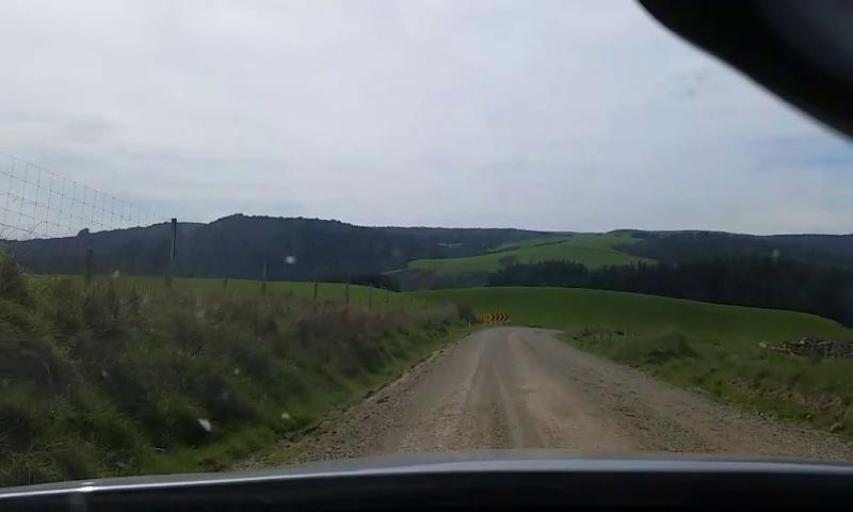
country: NZ
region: Otago
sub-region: Clutha District
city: Papatowai
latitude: -46.6292
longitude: 168.9835
